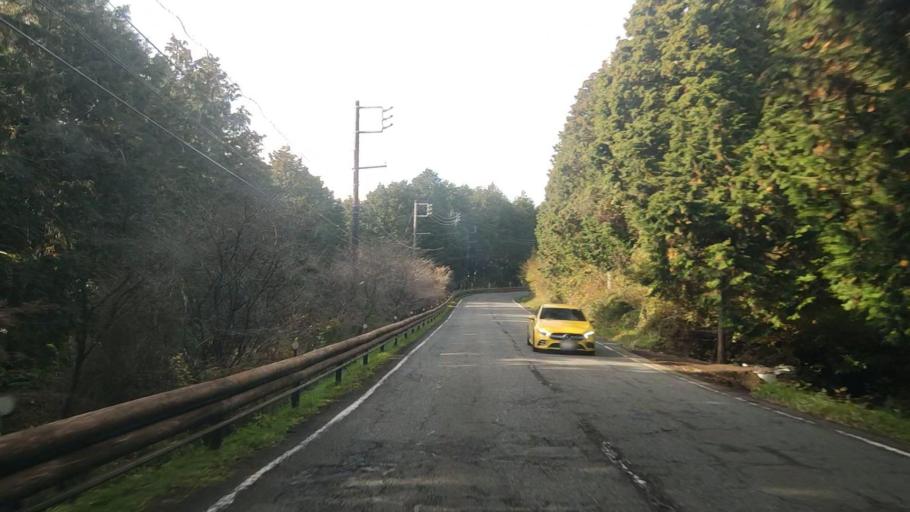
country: JP
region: Shizuoka
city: Fujinomiya
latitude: 35.2967
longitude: 138.6698
